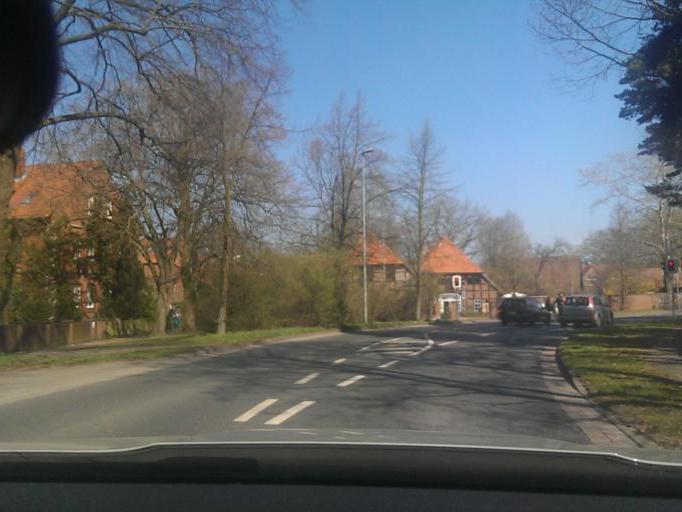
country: DE
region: Lower Saxony
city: Elze
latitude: 52.5208
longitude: 9.7520
